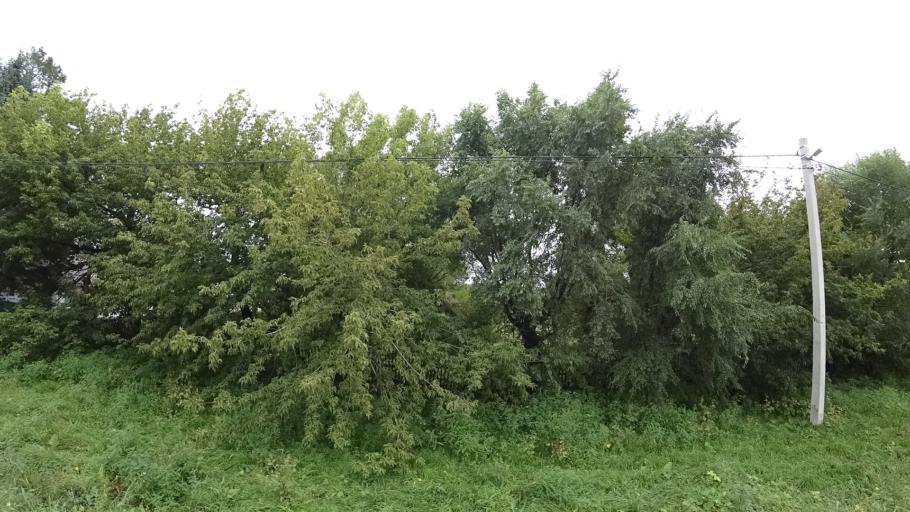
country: RU
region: Primorskiy
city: Monastyrishche
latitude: 44.0798
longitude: 132.5823
